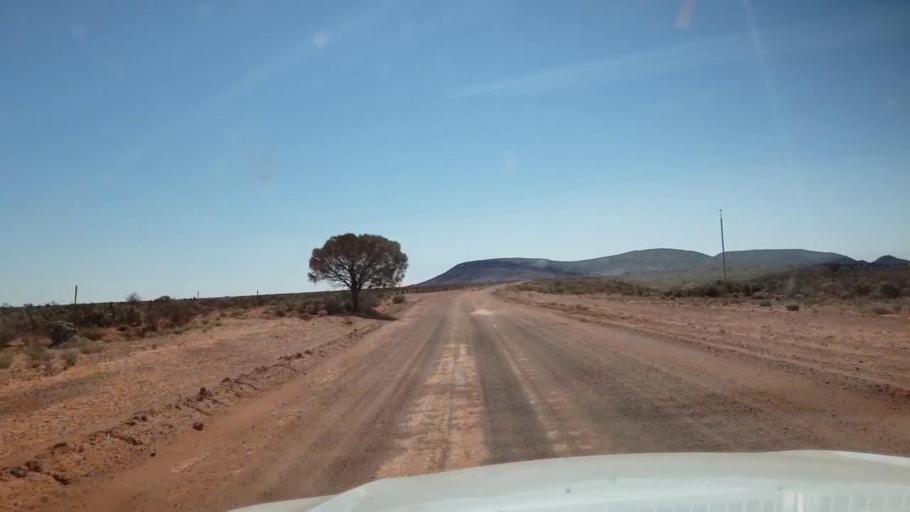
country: AU
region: South Australia
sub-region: Whyalla
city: Whyalla
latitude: -32.7102
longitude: 137.1401
